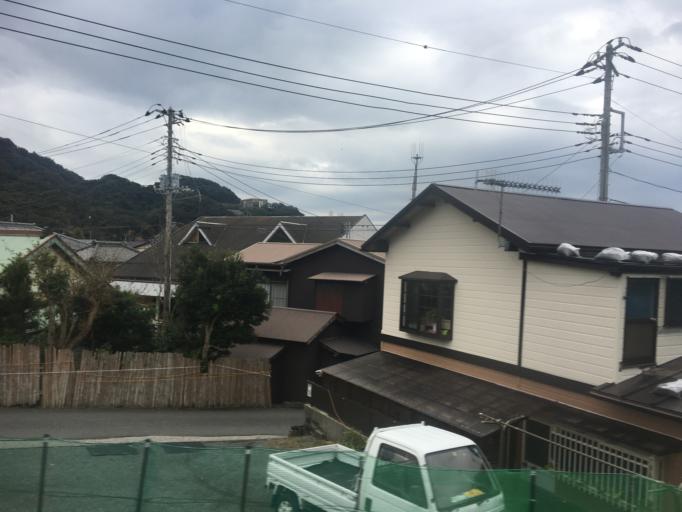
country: JP
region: Chiba
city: Futtsu
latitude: 35.1678
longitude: 139.8236
